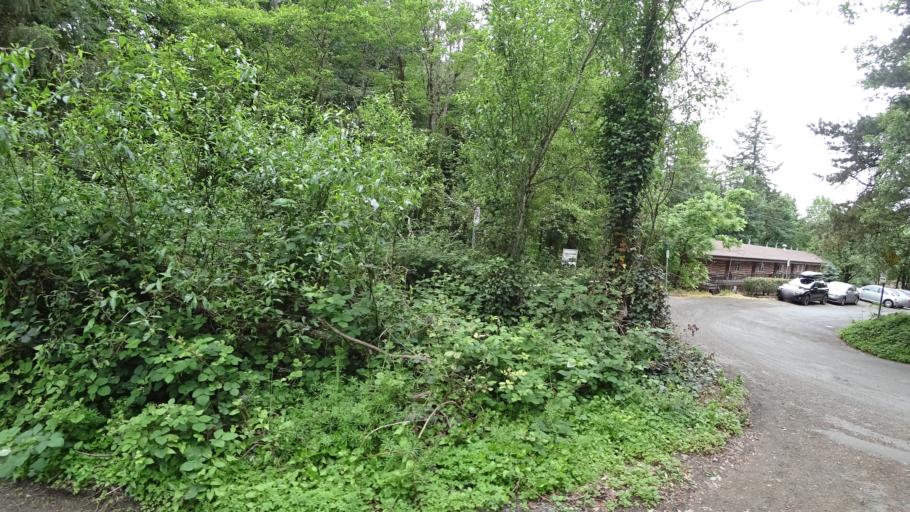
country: US
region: Oregon
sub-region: Multnomah County
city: Portland
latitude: 45.4998
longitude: -122.6931
